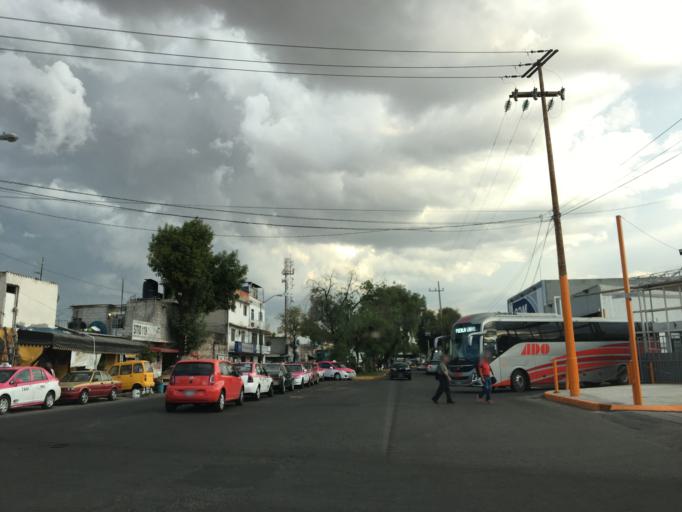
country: MX
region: Mexico
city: Colonia Lindavista
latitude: 19.4796
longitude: -99.1377
